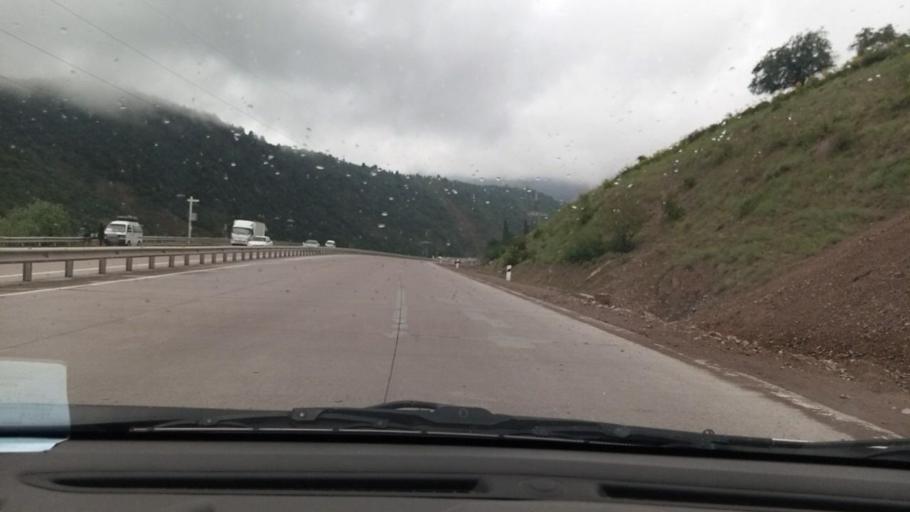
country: UZ
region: Toshkent
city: Angren
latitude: 41.1383
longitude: 70.4583
